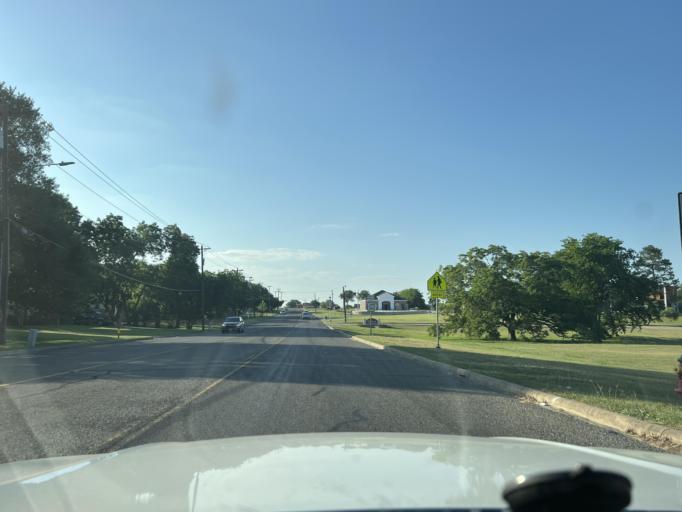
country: US
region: Texas
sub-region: Washington County
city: Brenham
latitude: 30.1776
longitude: -96.4006
